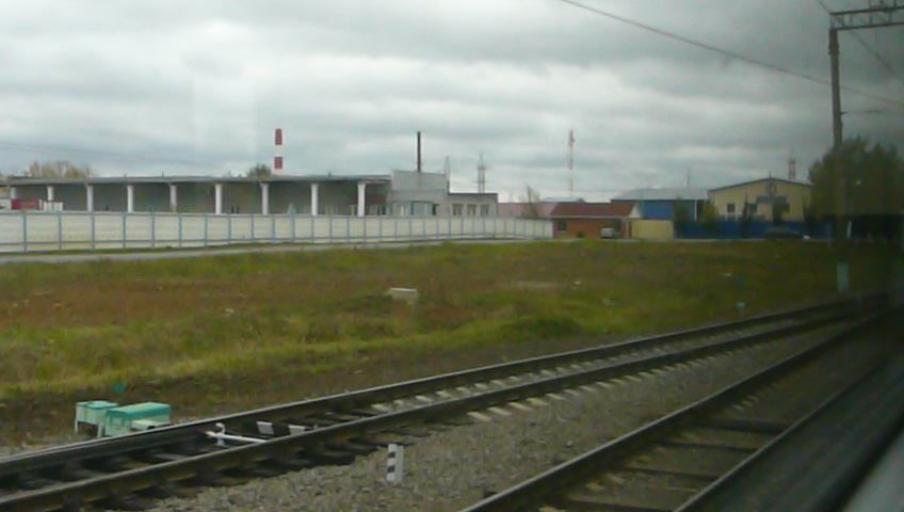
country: RU
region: Moskovskaya
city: Yegor'yevsk
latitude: 55.3931
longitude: 39.0067
